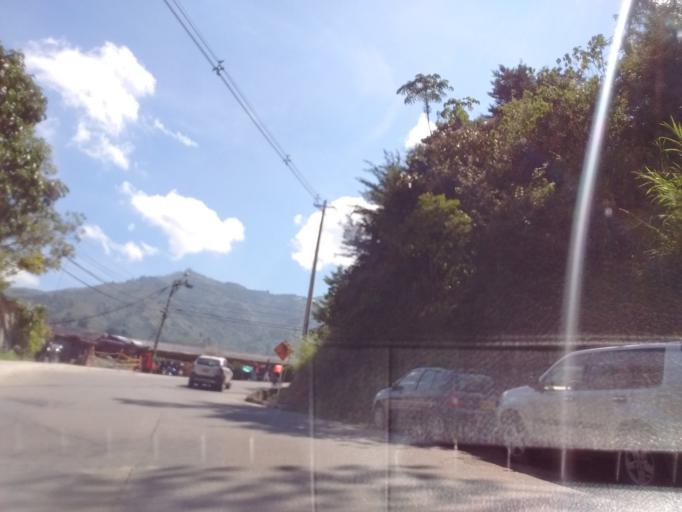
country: CO
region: Antioquia
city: Medellin
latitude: 6.2281
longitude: -75.5272
